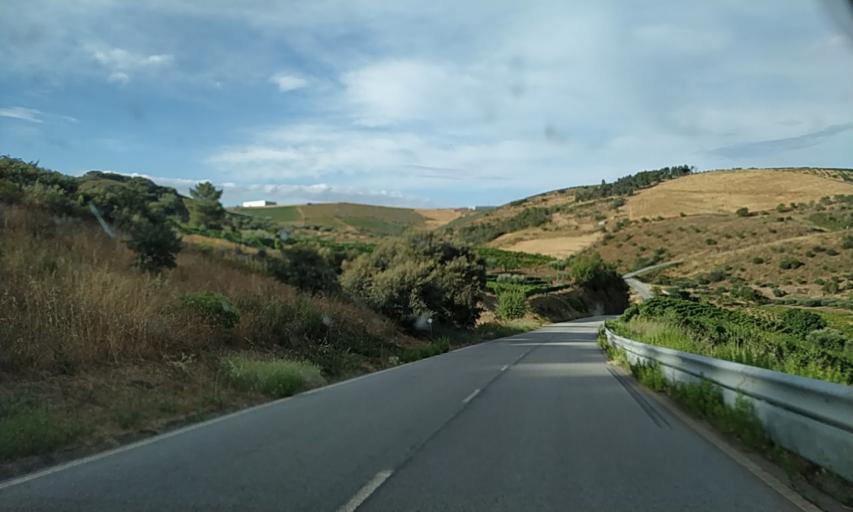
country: PT
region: Viseu
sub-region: Sao Joao da Pesqueira
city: Sao Joao da Pesqueira
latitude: 41.1407
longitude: -7.4349
